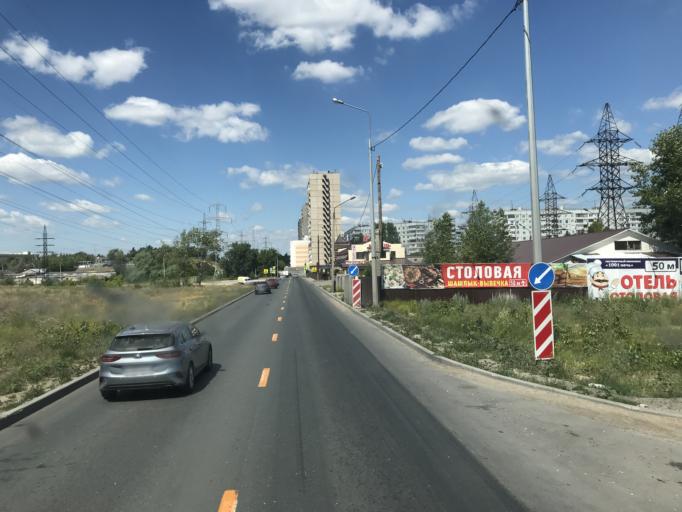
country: RU
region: Samara
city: Zhigulevsk
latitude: 53.4690
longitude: 49.5129
